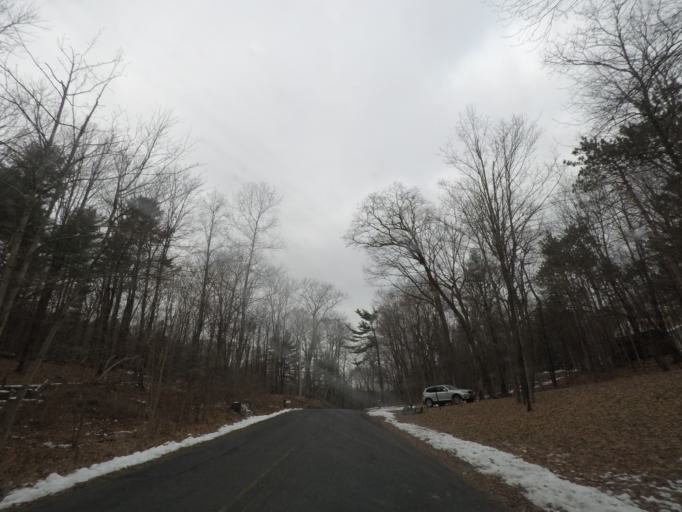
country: US
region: New York
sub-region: Rensselaer County
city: East Greenbush
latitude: 42.5909
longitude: -73.6464
